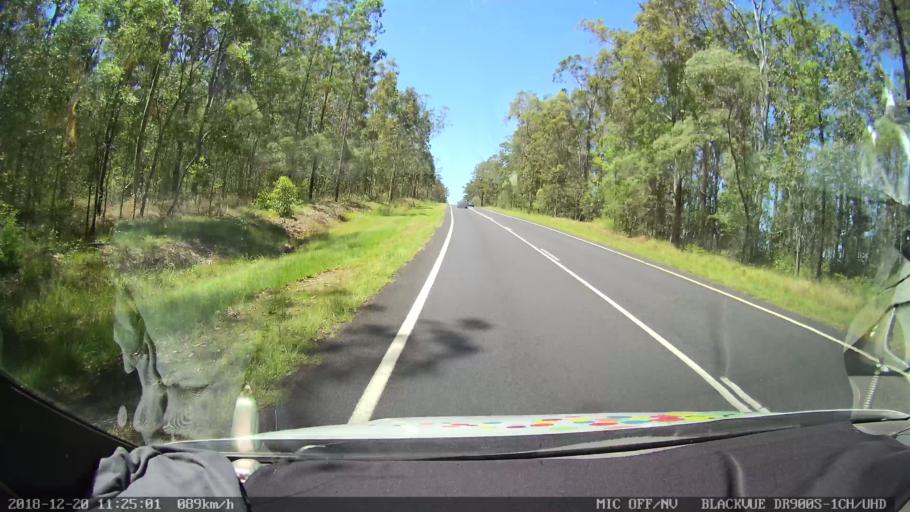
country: AU
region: New South Wales
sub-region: Richmond Valley
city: Casino
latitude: -29.0821
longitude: 153.0004
